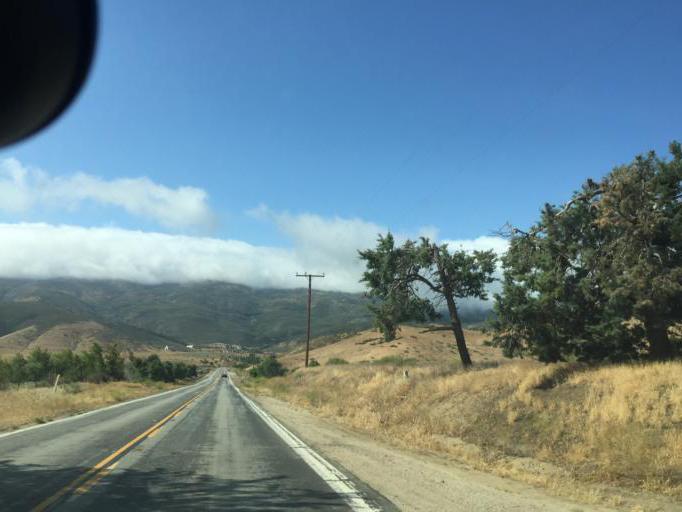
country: US
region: California
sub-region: Los Angeles County
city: Leona Valley
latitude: 34.6031
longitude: -118.2711
